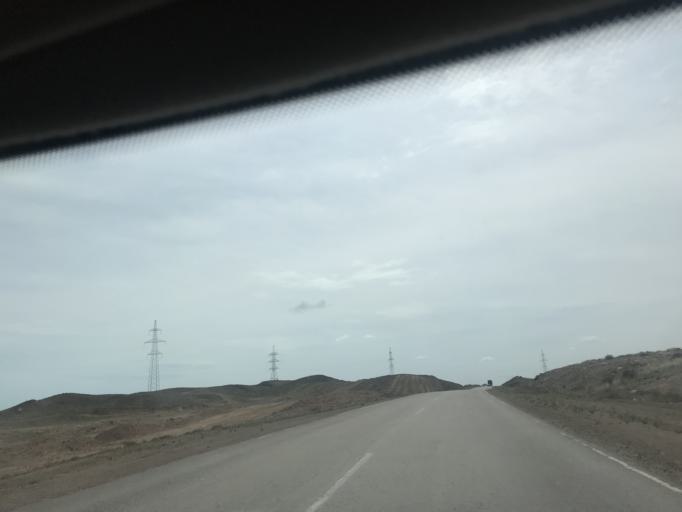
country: KZ
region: Zhambyl
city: Mynaral
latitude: 45.3550
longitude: 73.6825
